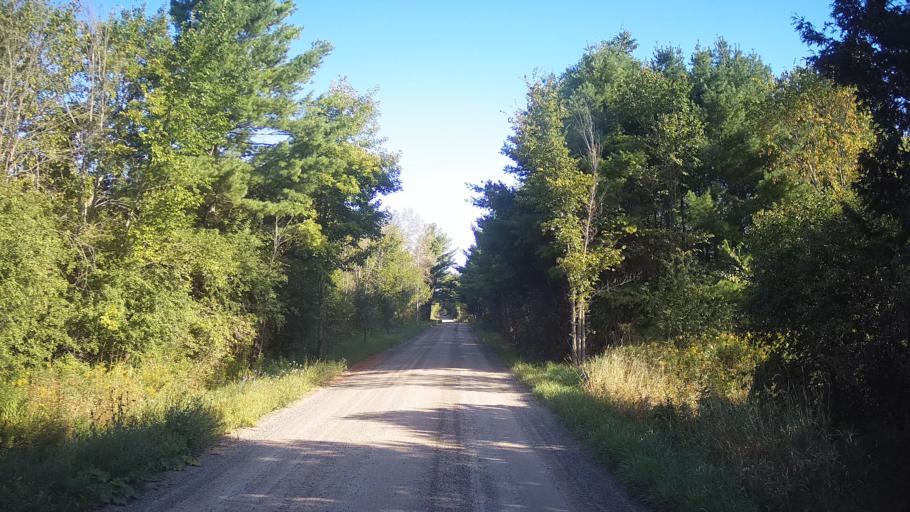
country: US
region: New York
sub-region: Jefferson County
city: Alexandria Bay
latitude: 44.4107
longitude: -75.9764
